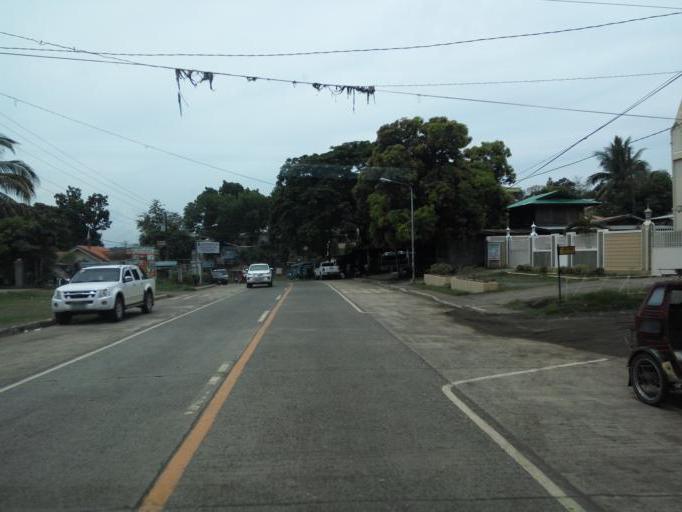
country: PH
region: Cagayan Valley
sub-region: Province of Quirino
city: Diffun
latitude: 16.5920
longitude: 121.5027
